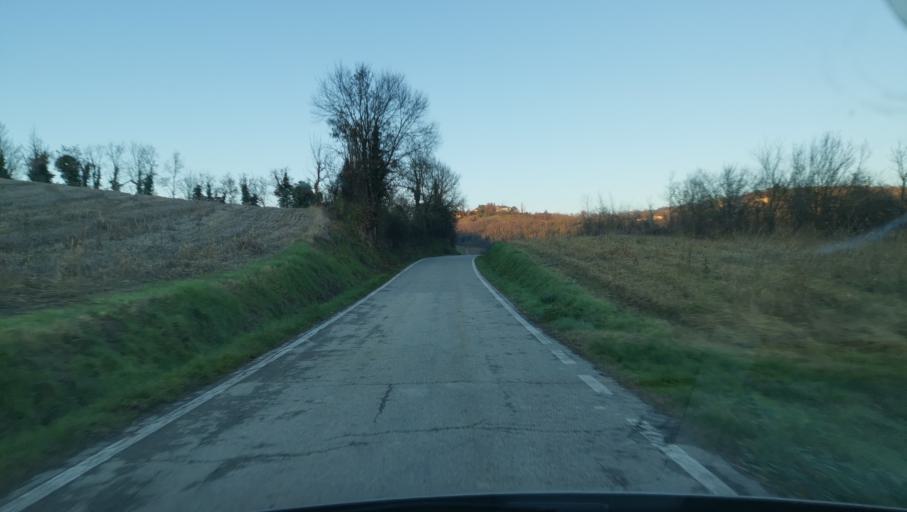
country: IT
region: Piedmont
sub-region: Provincia di Asti
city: Moncucco Torinese
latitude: 45.0656
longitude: 7.9422
